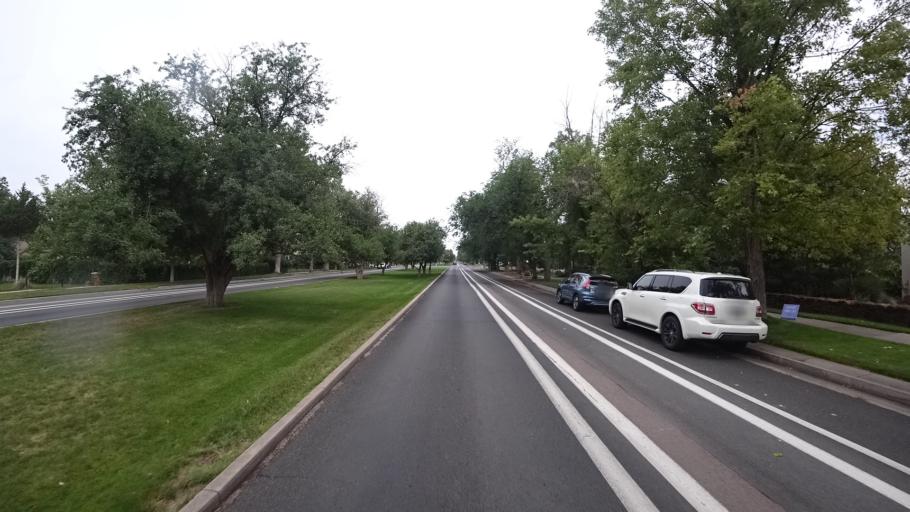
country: US
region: Colorado
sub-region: El Paso County
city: Colorado Springs
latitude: 38.8593
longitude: -104.8239
